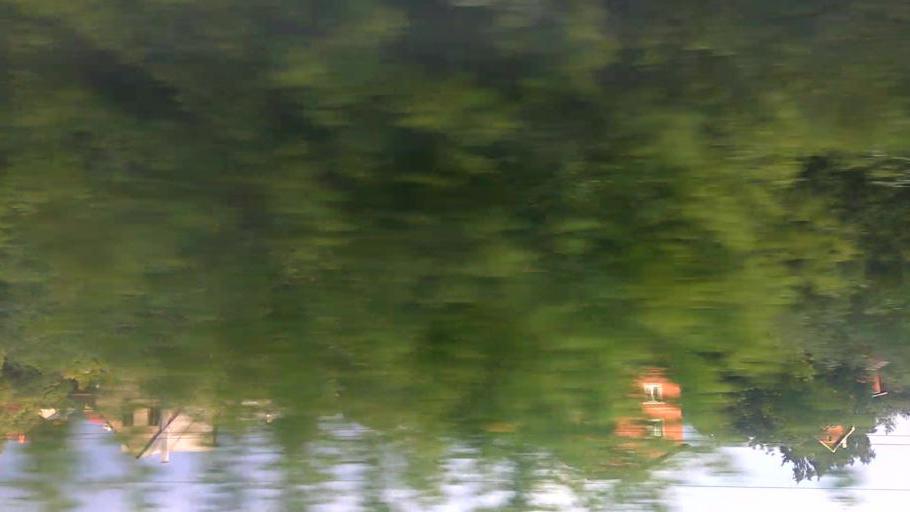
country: RU
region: Moskovskaya
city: Stupino
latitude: 54.8939
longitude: 38.0936
